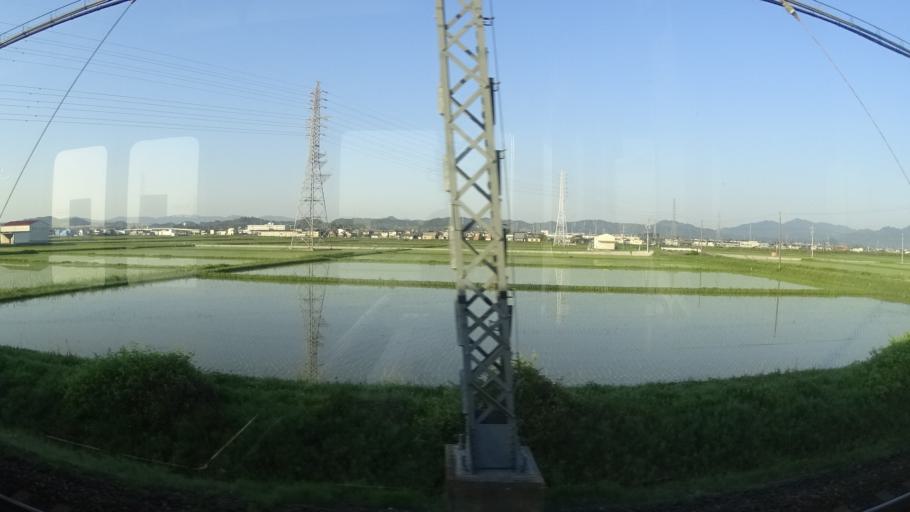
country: JP
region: Mie
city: Hisai-motomachi
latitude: 34.5619
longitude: 136.5529
